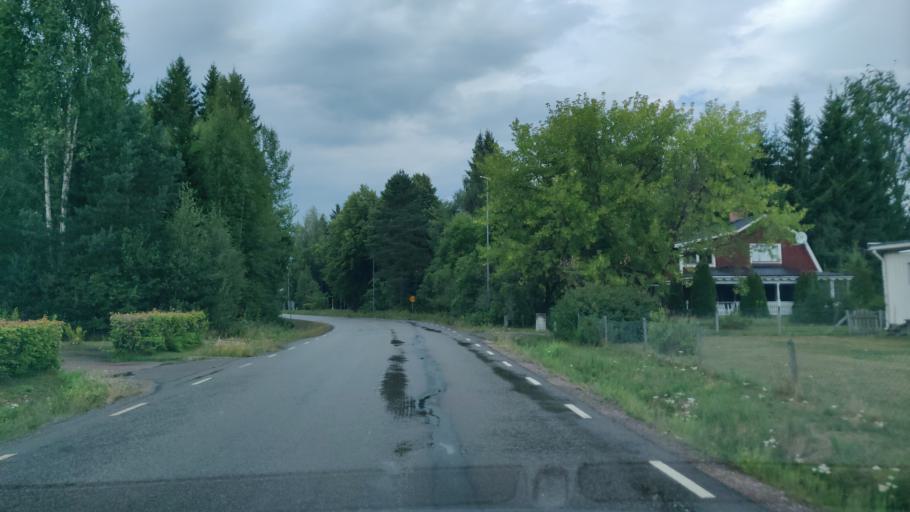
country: SE
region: Vaermland
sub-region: Munkfors Kommun
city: Munkfors
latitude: 59.8580
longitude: 13.5524
